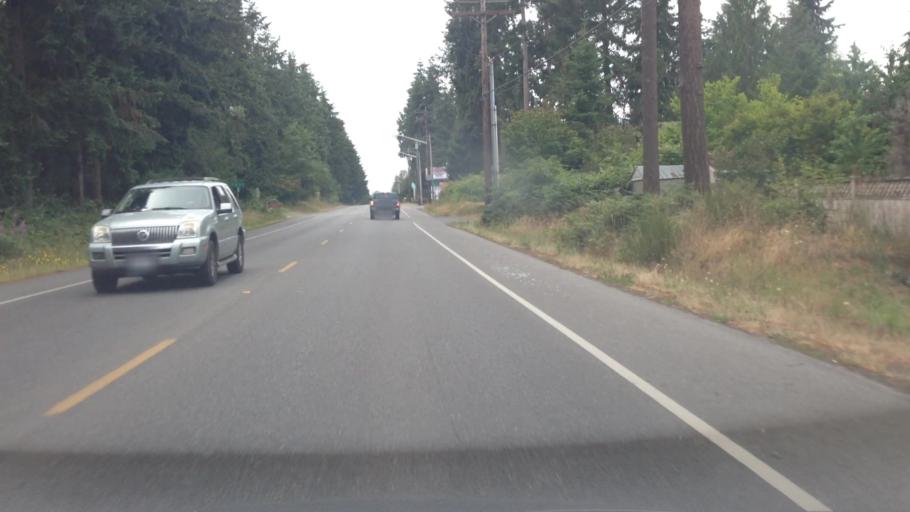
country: US
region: Washington
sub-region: Pierce County
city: South Hill
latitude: 47.1111
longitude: -122.3013
